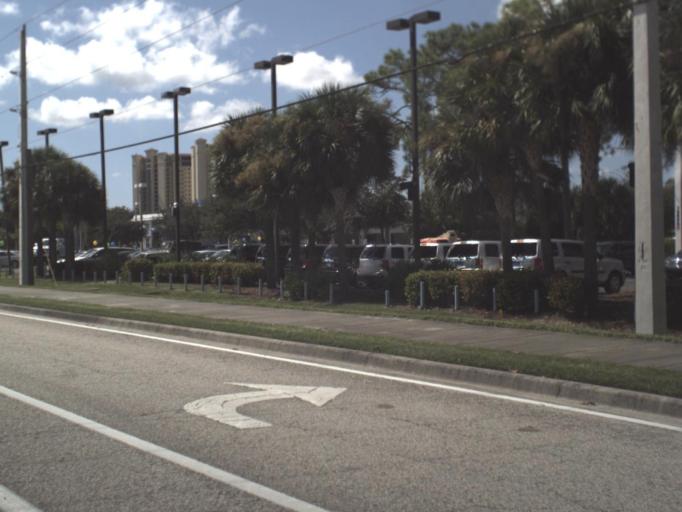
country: US
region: Florida
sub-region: Lee County
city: Villas
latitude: 26.5398
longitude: -81.8715
